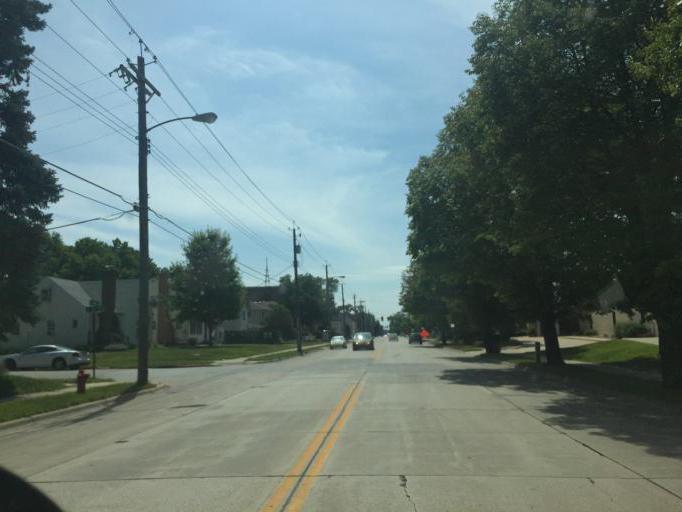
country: US
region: Minnesota
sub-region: Olmsted County
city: Rochester
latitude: 44.0162
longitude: -92.4588
